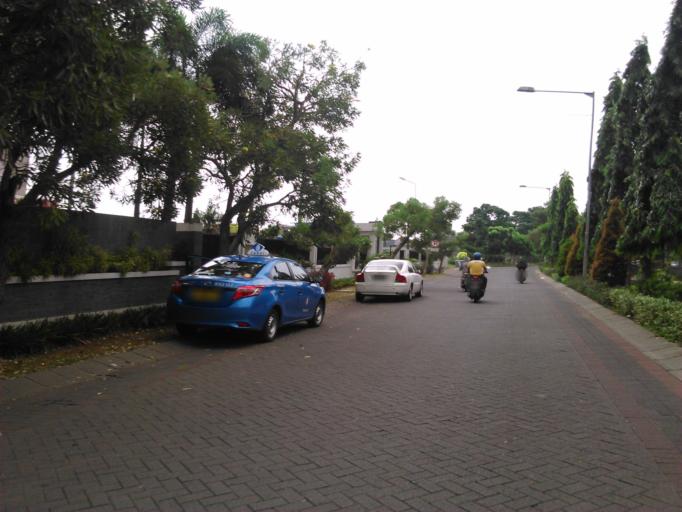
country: ID
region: East Java
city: Semampir
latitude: -7.2883
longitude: 112.7875
